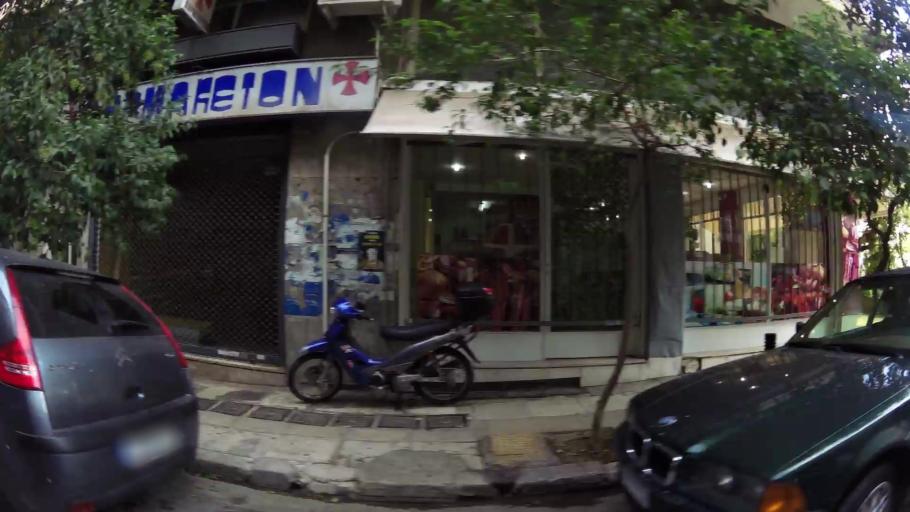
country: GR
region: Attica
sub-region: Nomarchia Athinas
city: Kipseli
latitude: 37.9984
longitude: 23.7378
